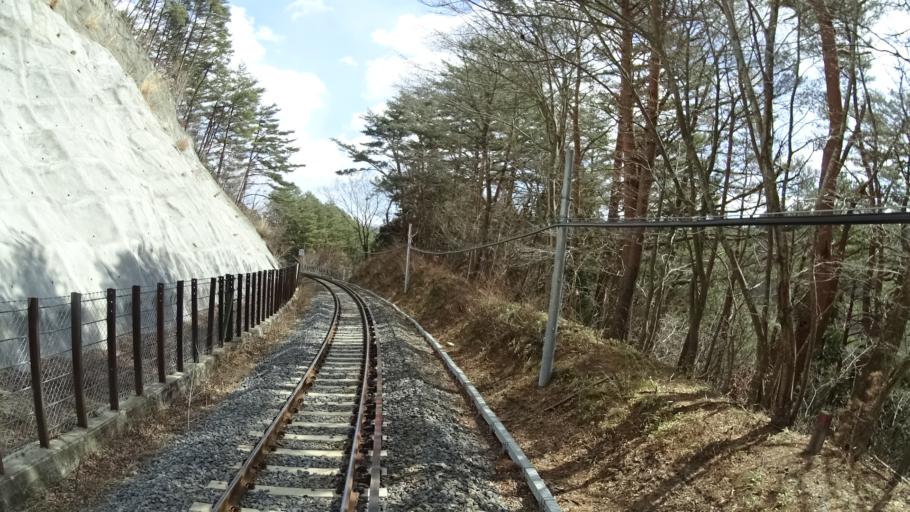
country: JP
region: Iwate
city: Yamada
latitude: 39.4757
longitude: 141.9264
